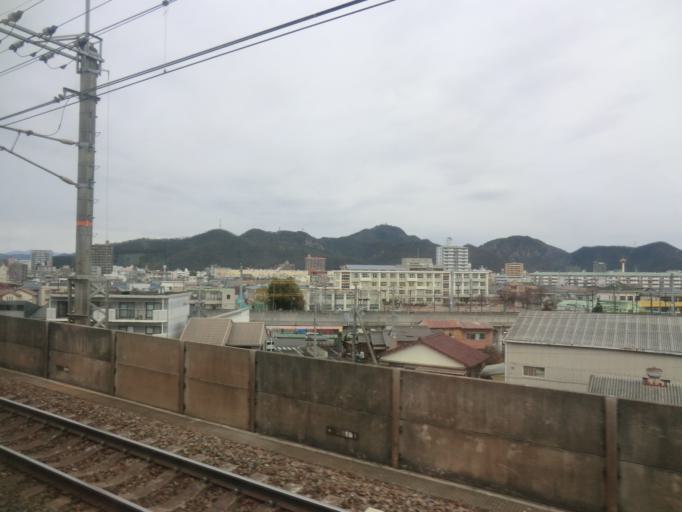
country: JP
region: Gifu
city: Gifu-shi
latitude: 35.4066
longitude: 136.7689
